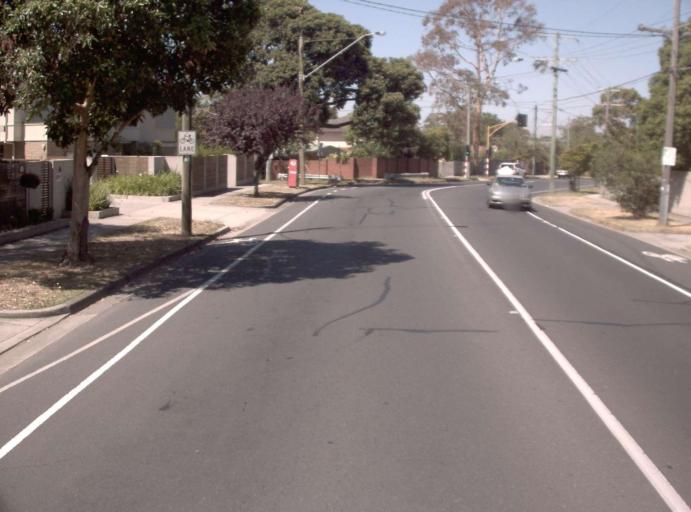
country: AU
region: Victoria
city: Beaumaris
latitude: -37.9782
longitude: 145.0379
